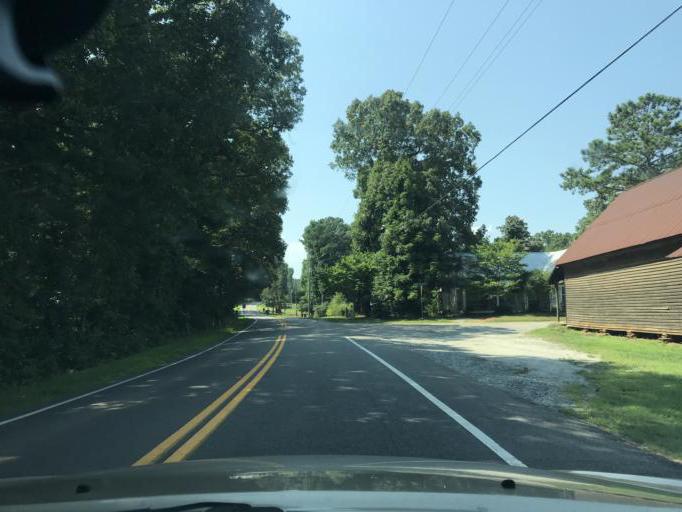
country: US
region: Georgia
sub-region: Hall County
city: Flowery Branch
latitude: 34.2370
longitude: -83.9977
